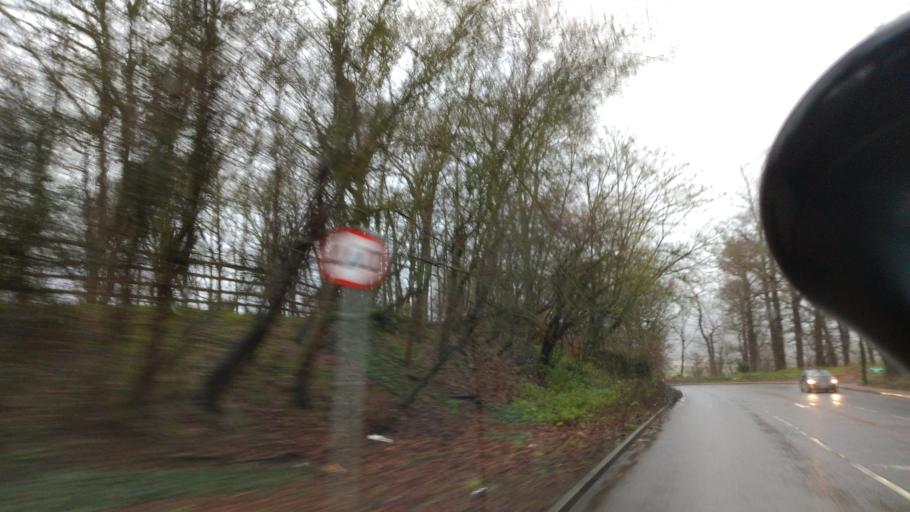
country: GB
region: England
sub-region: West Sussex
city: Arundel
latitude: 50.8464
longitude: -0.5409
